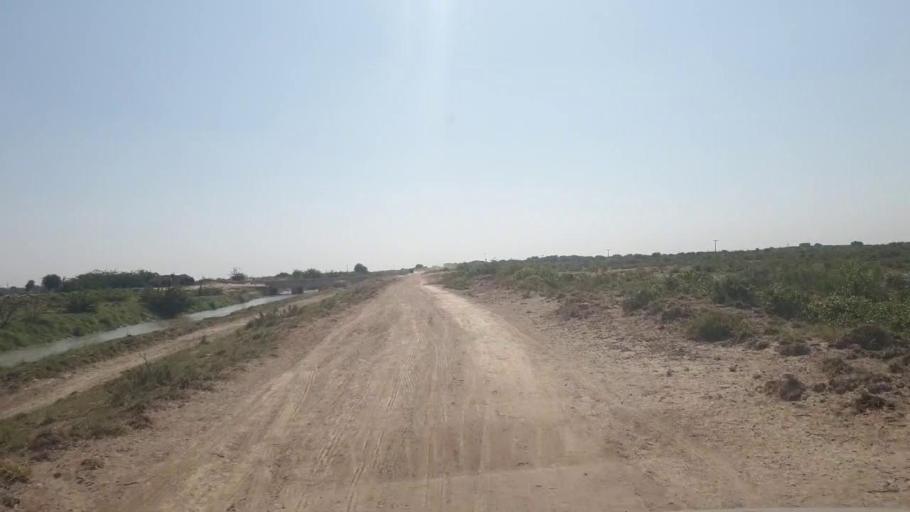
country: PK
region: Sindh
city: Digri
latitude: 24.9227
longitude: 69.1646
